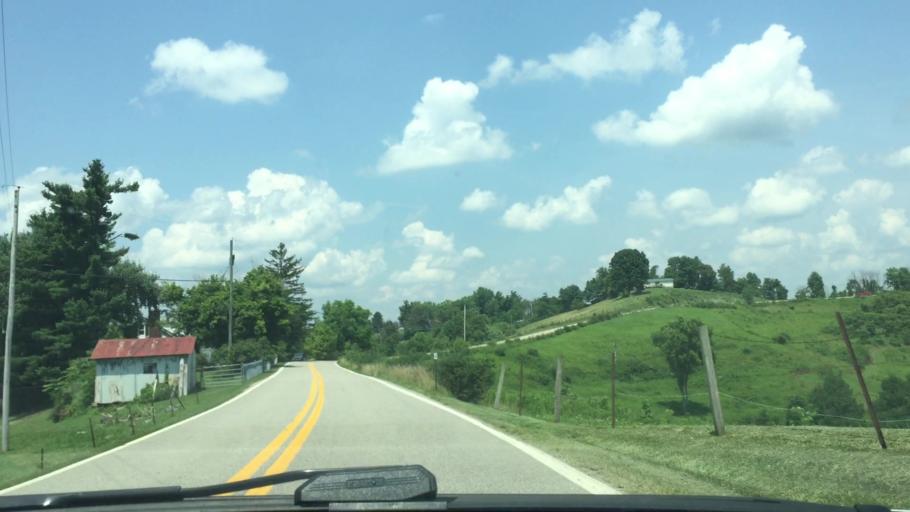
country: US
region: West Virginia
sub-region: Wetzel County
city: New Martinsville
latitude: 39.6958
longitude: -80.7708
